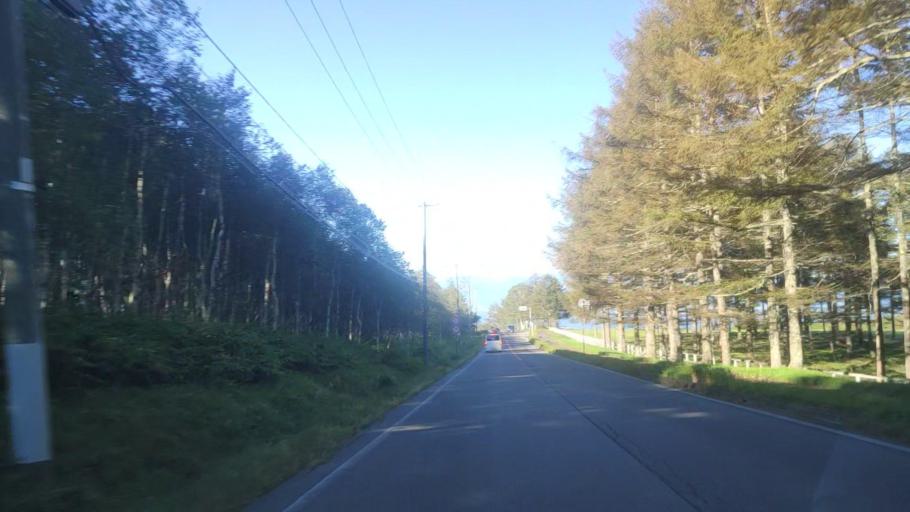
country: JP
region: Nagano
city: Kamimaruko
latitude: 36.1517
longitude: 138.2791
